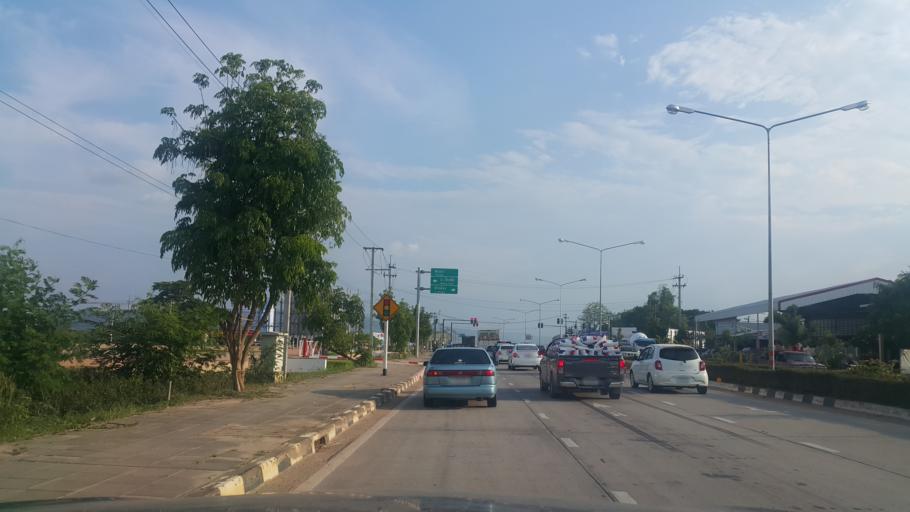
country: TH
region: Chiang Rai
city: Chiang Rai
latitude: 19.8963
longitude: 99.8567
